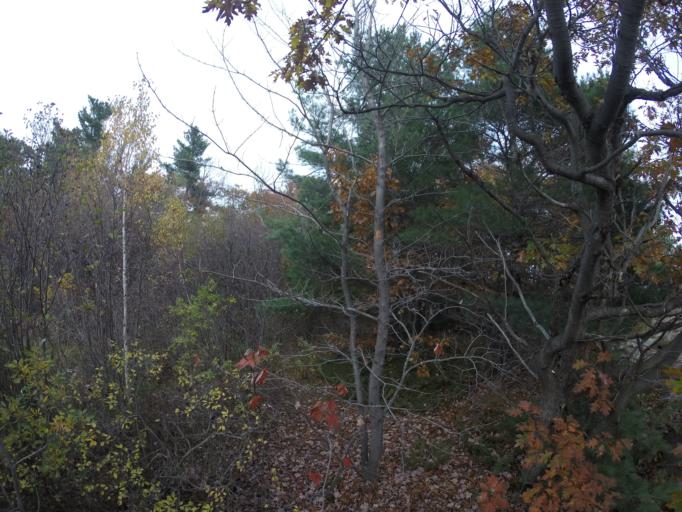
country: CA
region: Ontario
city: Espanola
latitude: 45.9684
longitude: -81.5003
